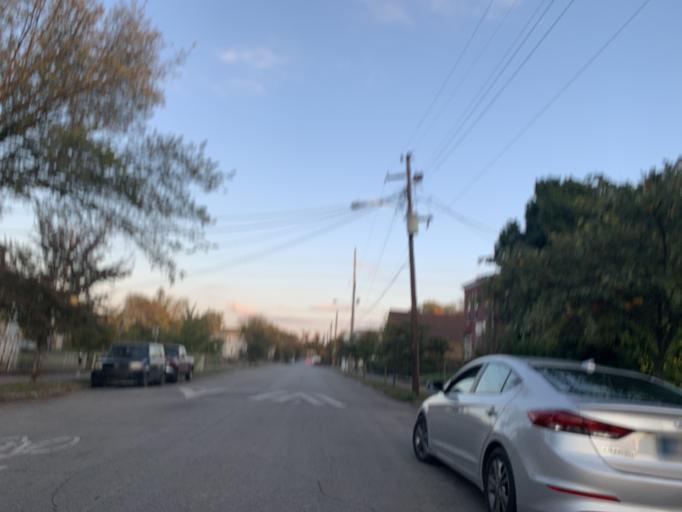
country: US
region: Kentucky
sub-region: Jefferson County
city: Louisville
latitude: 38.2535
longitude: -85.7887
